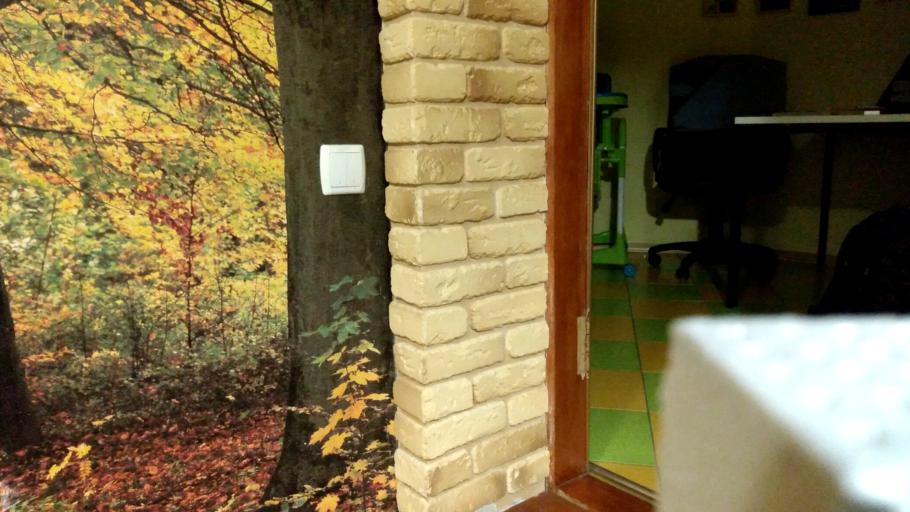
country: RU
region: Arkhangelskaya
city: Kargopol'
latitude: 61.5024
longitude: 37.7793
